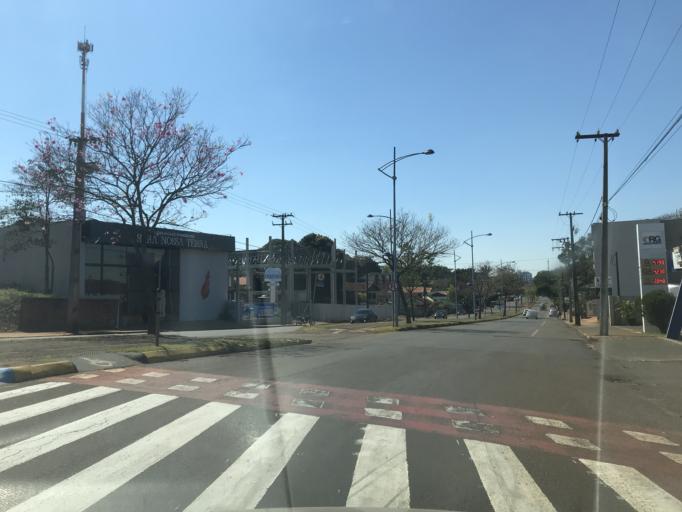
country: BR
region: Parana
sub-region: Toledo
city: Toledo
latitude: -24.7268
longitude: -53.7359
